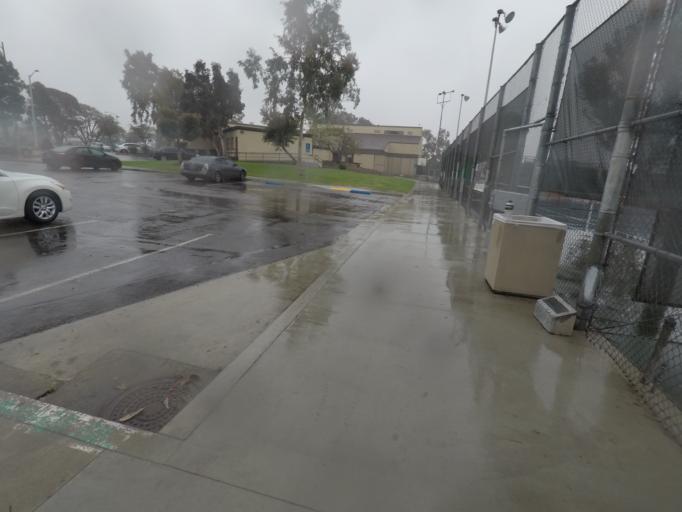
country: US
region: California
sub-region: San Diego County
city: San Diego
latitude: 32.7931
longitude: -117.1701
